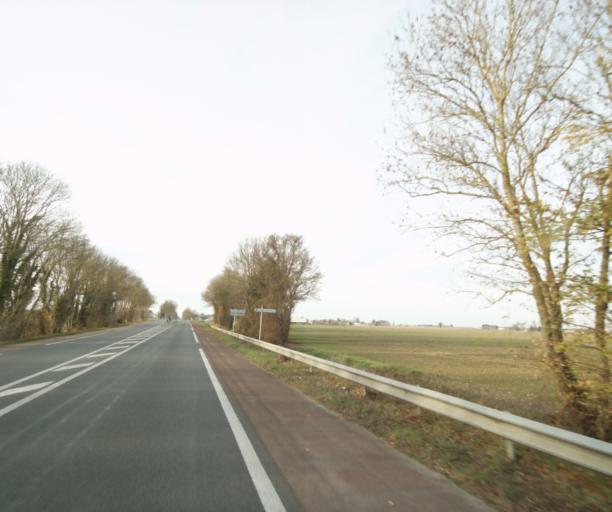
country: FR
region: Poitou-Charentes
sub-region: Departement de la Charente-Maritime
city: Nieul-les-Saintes
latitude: 45.7990
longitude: -0.7416
